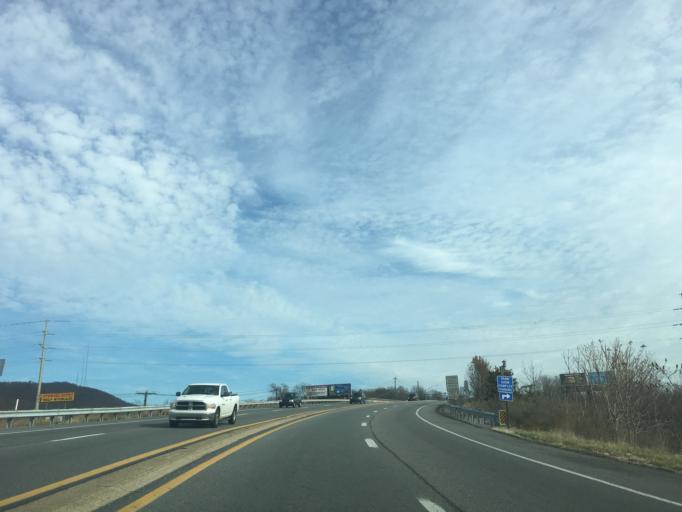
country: US
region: Pennsylvania
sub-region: Perry County
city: Marysville
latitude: 40.3257
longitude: -76.8954
